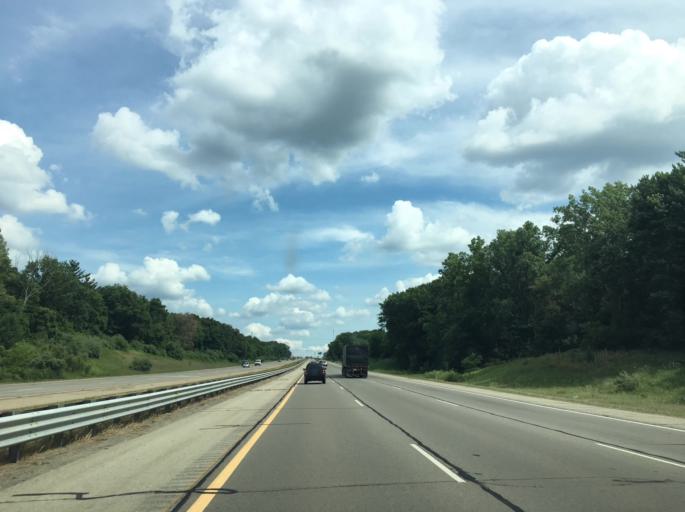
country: US
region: Michigan
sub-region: Oakland County
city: Holly
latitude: 42.7986
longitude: -83.5532
